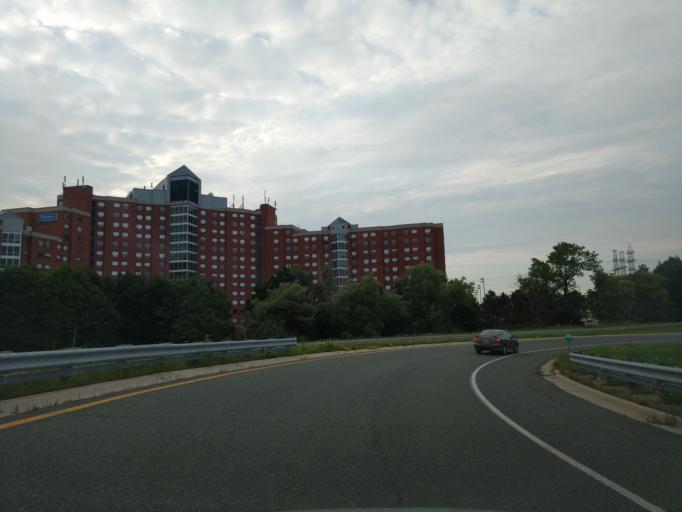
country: CA
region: Ontario
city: Willowdale
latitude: 43.7954
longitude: -79.3452
